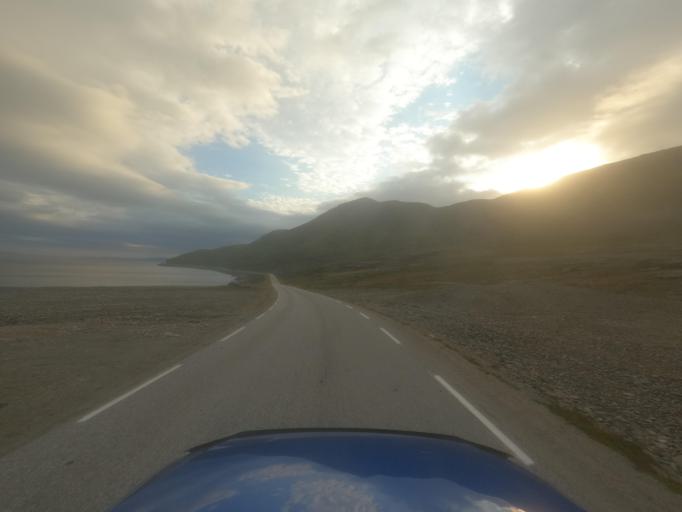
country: NO
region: Finnmark Fylke
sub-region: Nordkapp
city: Honningsvag
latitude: 70.6969
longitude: 25.5081
